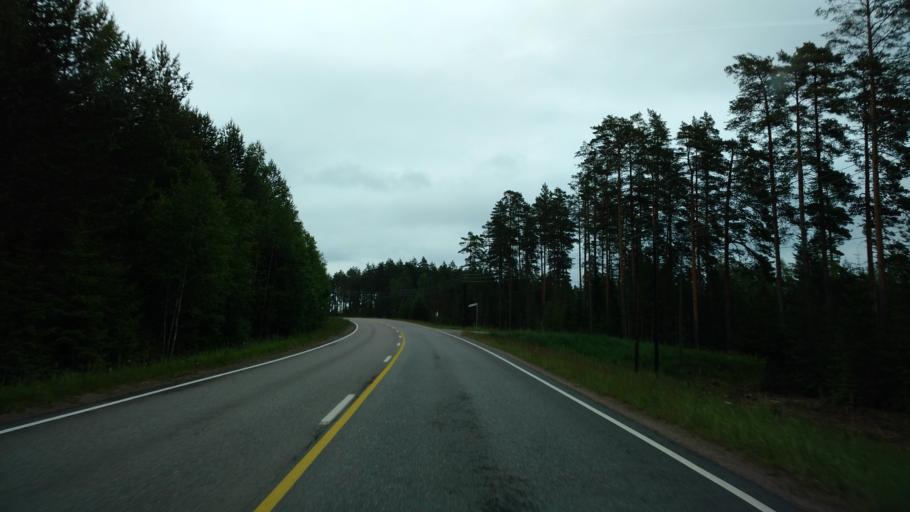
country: FI
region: Varsinais-Suomi
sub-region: Salo
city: Kiikala
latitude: 60.4218
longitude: 23.5912
